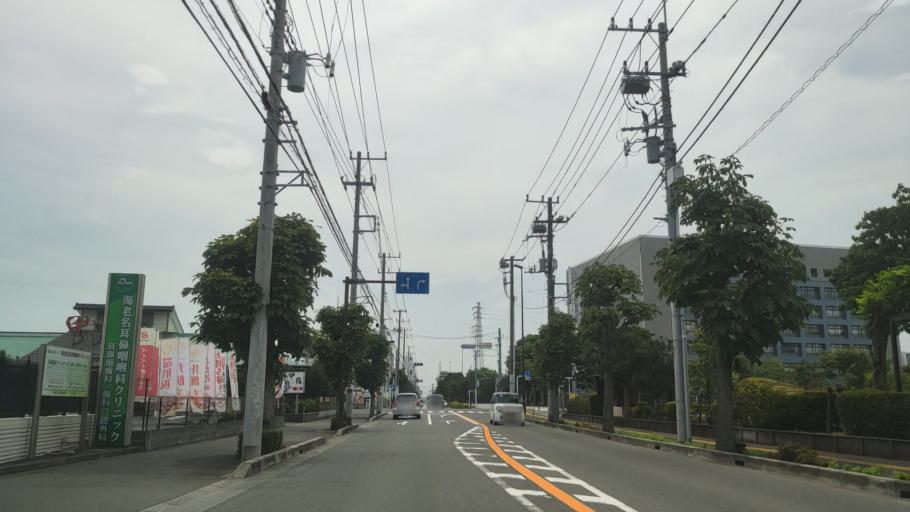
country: JP
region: Kanagawa
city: Atsugi
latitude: 35.4478
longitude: 139.3917
